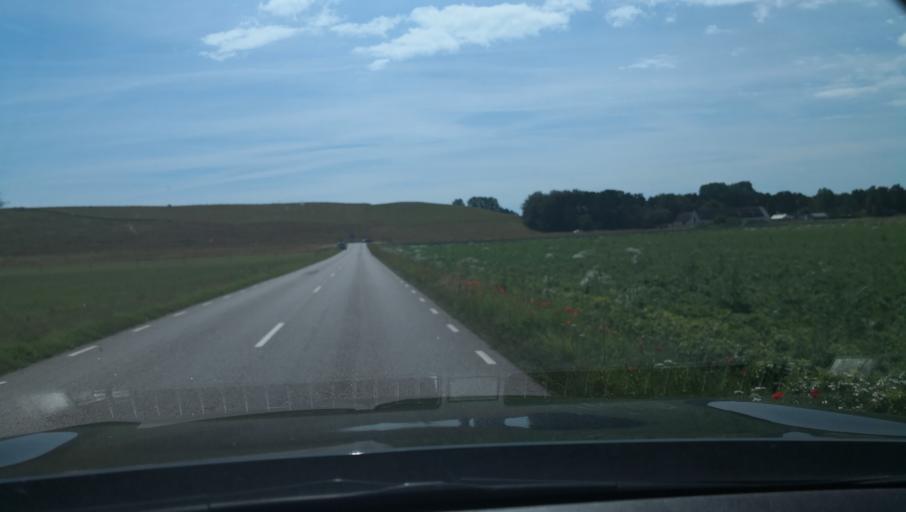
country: SE
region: Skane
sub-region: Ystads Kommun
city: Kopingebro
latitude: 55.3950
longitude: 14.1131
